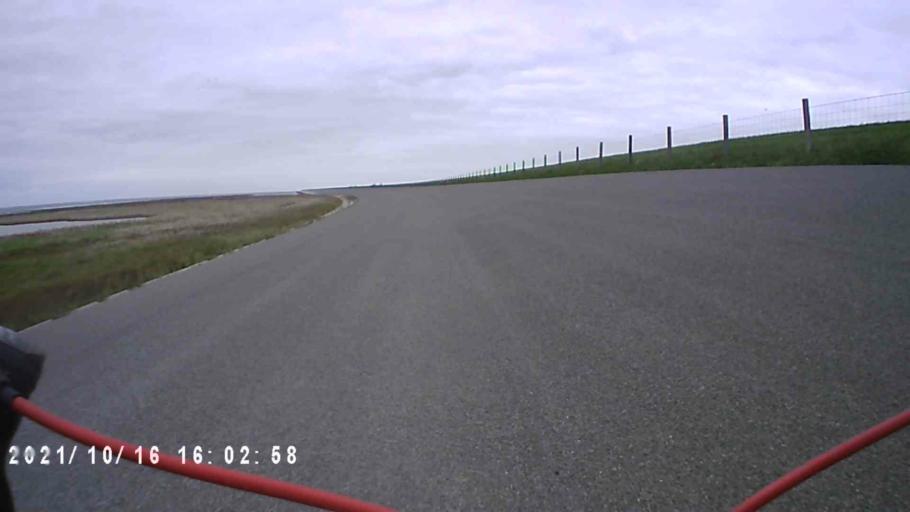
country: NL
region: Friesland
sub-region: Gemeente Dongeradeel
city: Anjum
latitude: 53.4017
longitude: 6.1323
